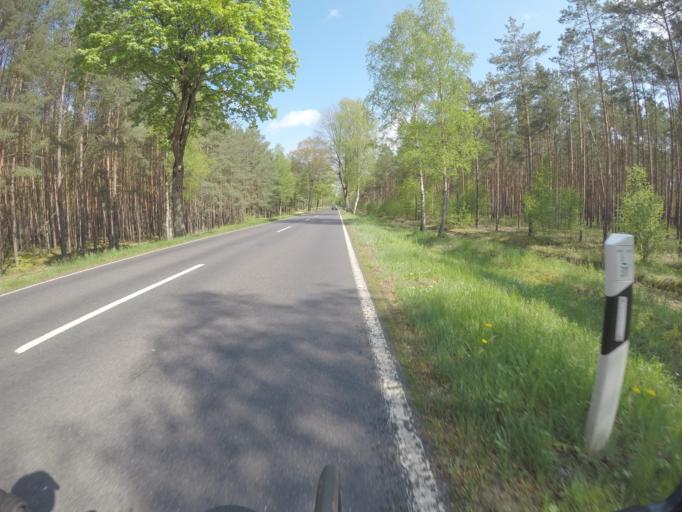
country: DE
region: Brandenburg
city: Marienwerder
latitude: 52.8060
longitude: 13.5533
